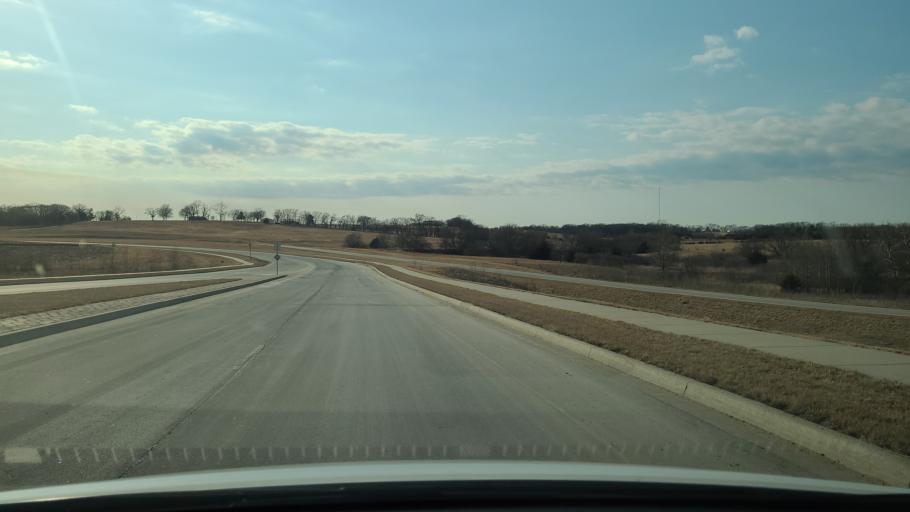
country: US
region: Kansas
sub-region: Douglas County
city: Lawrence
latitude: 38.9572
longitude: -95.3387
